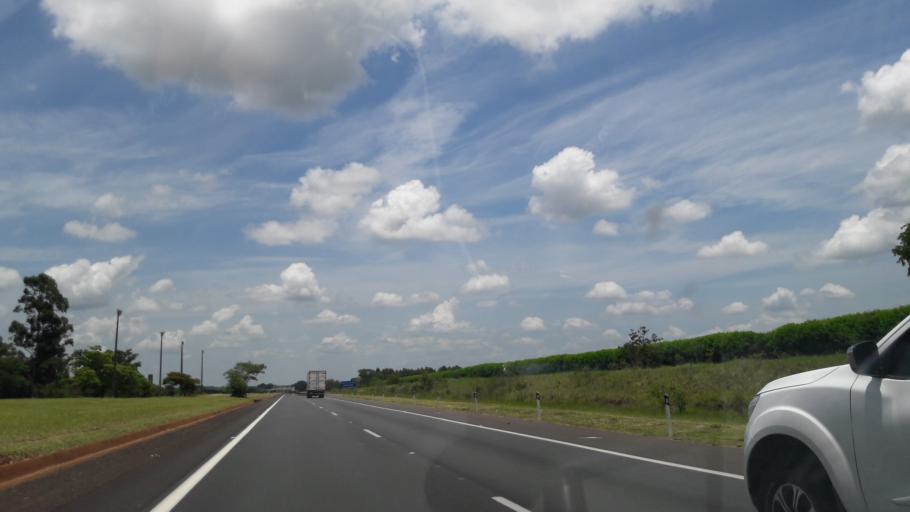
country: BR
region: Sao Paulo
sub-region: Avare
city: Avare
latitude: -22.9547
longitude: -48.8678
